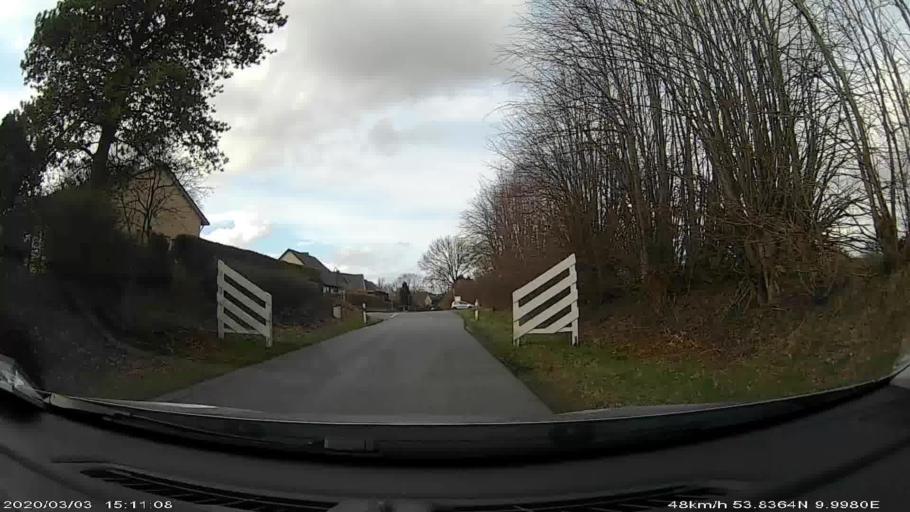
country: DE
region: Schleswig-Holstein
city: Oersdorf
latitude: 53.8361
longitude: 9.9982
